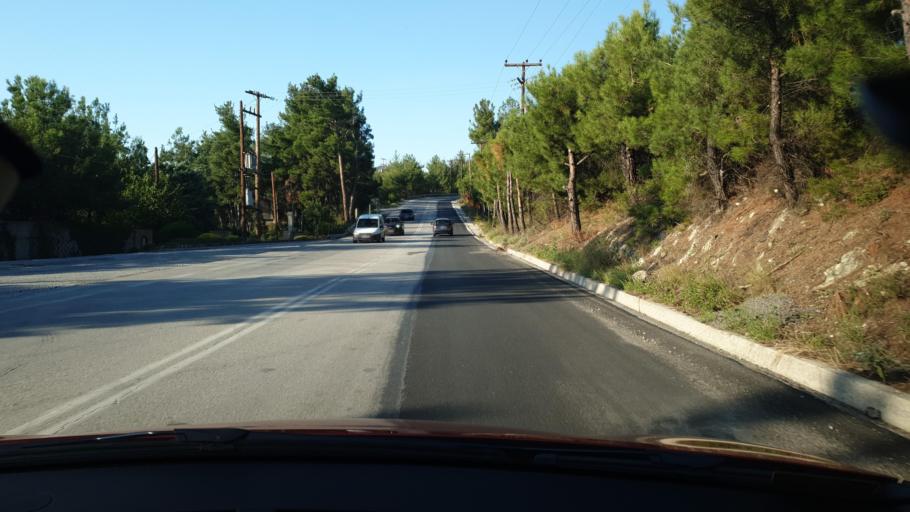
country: GR
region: Central Macedonia
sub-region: Nomos Thessalonikis
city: Panorama
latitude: 40.6064
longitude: 23.0514
